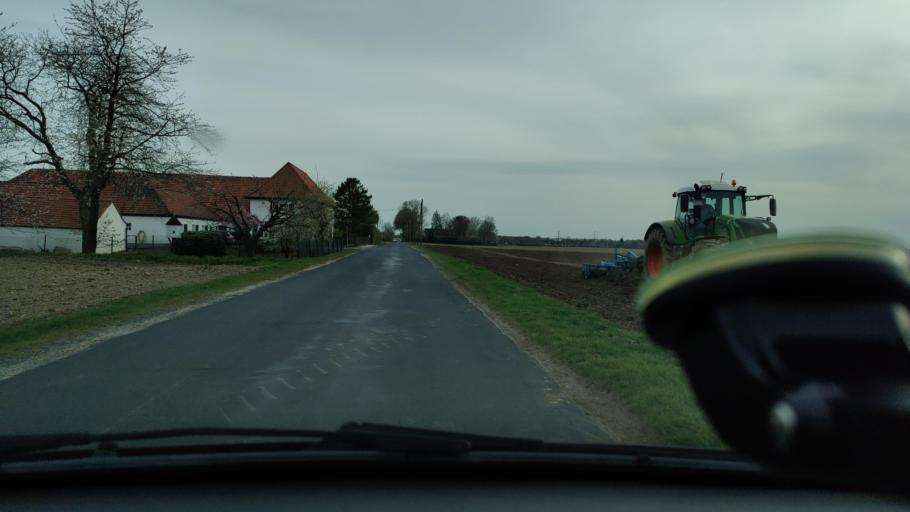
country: DE
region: North Rhine-Westphalia
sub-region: Regierungsbezirk Dusseldorf
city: Goch
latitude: 51.7081
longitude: 6.1808
